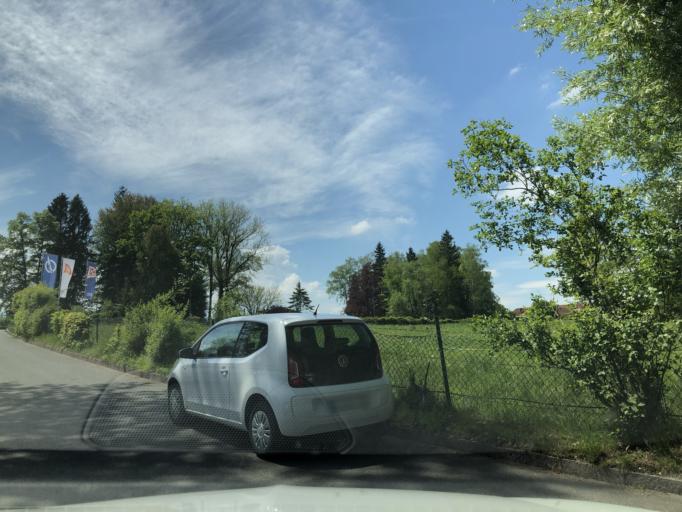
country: DE
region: Bavaria
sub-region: Upper Bavaria
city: Prien am Chiemsee
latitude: 47.8478
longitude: 12.3689
